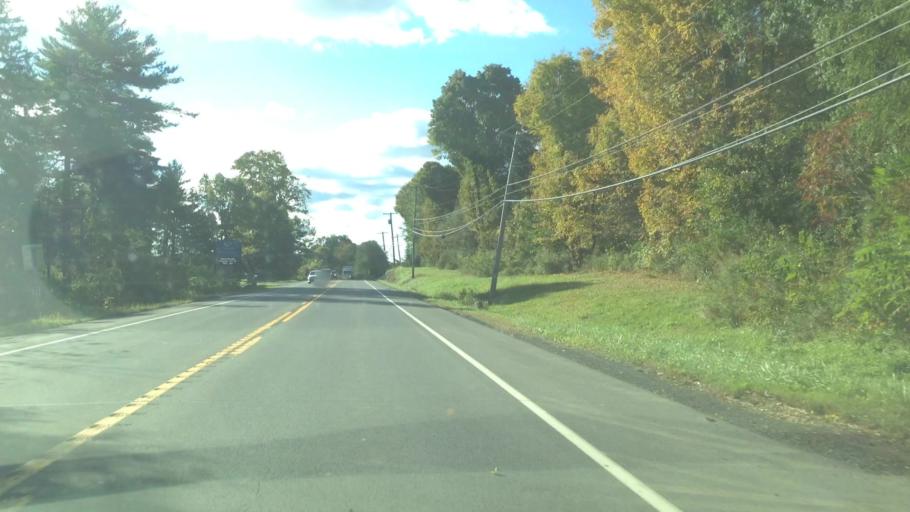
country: US
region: New York
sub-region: Dutchess County
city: Hyde Park
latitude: 41.8372
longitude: -73.9653
